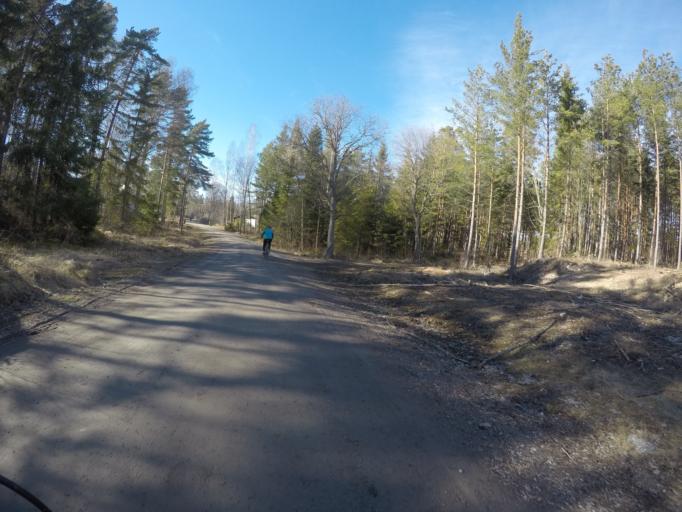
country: SE
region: Soedermanland
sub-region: Eskilstuna Kommun
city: Torshalla
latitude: 59.4250
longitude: 16.4456
